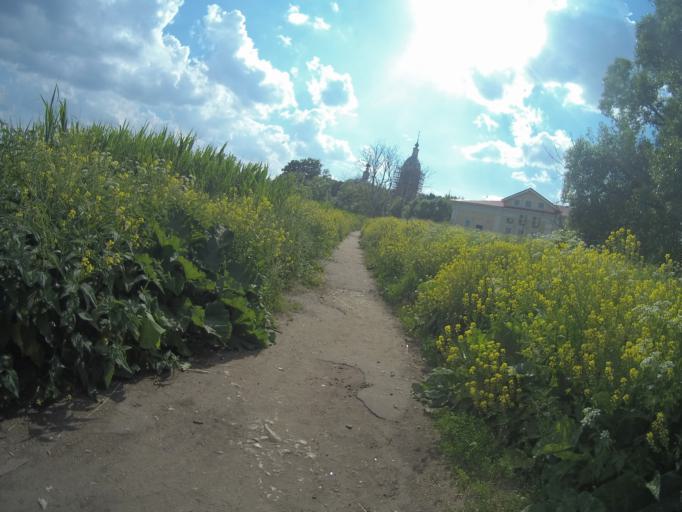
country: RU
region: Vladimir
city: Suzdal'
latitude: 56.4099
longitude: 40.4492
